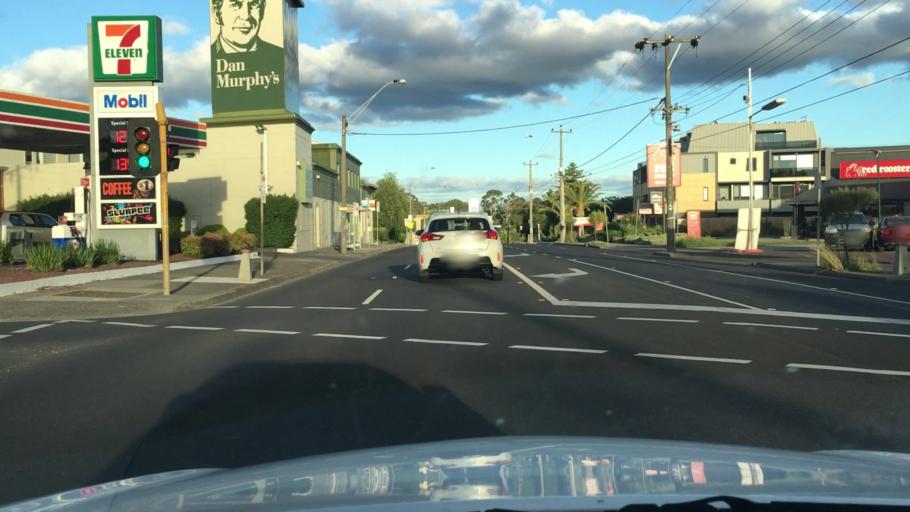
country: AU
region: Victoria
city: Alphington
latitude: -37.7805
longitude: 145.0323
